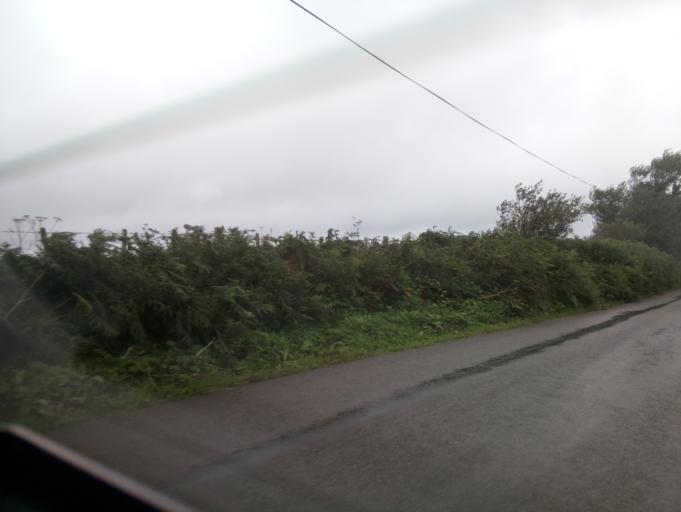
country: GB
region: England
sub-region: Devon
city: Kingsbridge
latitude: 50.3245
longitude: -3.7002
